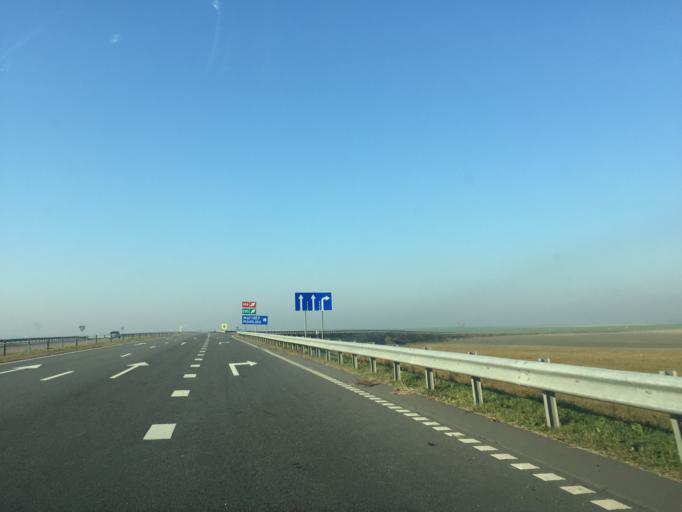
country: BY
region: Gomel
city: Kastsyukowka
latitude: 52.4908
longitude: 30.8261
